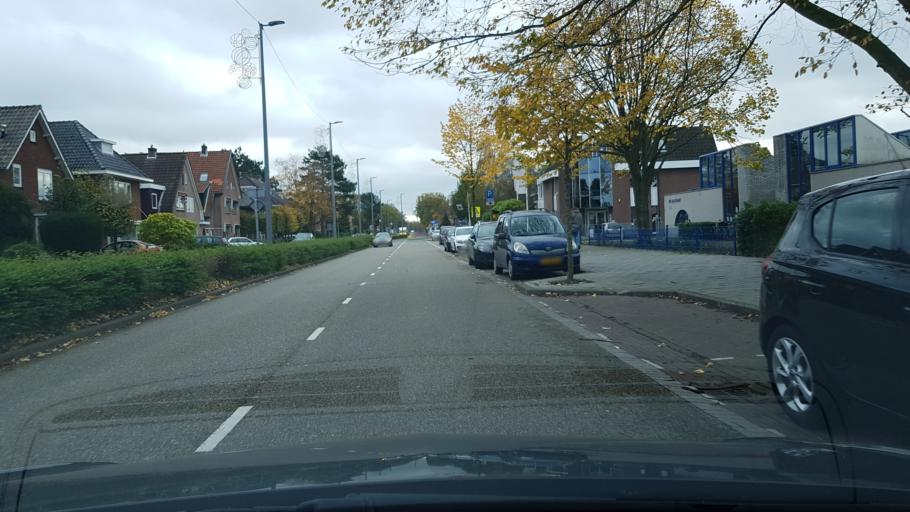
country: NL
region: North Holland
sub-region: Gemeente Haarlemmermeer
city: Hoofddorp
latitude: 52.3024
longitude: 4.6987
